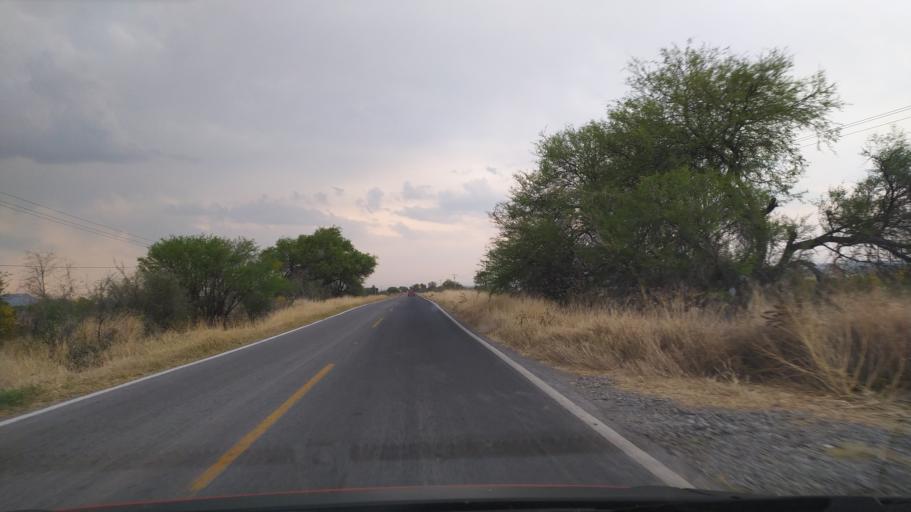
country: MX
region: Guanajuato
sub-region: San Francisco del Rincon
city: San Ignacio de Hidalgo
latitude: 20.8348
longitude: -101.8990
